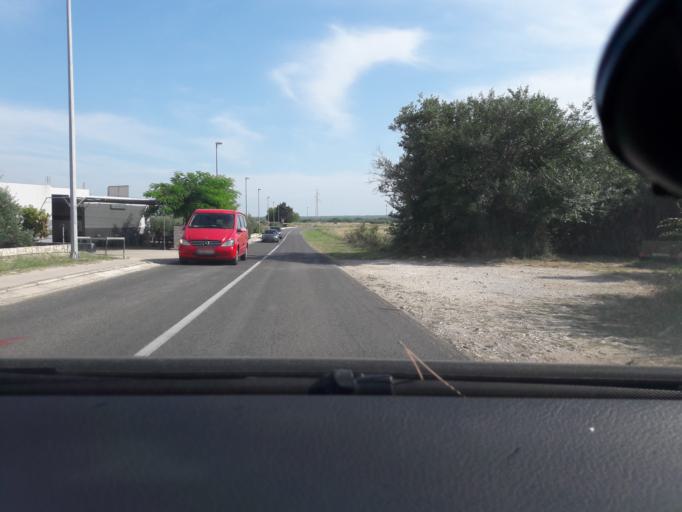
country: HR
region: Zadarska
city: Nin
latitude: 44.2363
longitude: 15.1816
